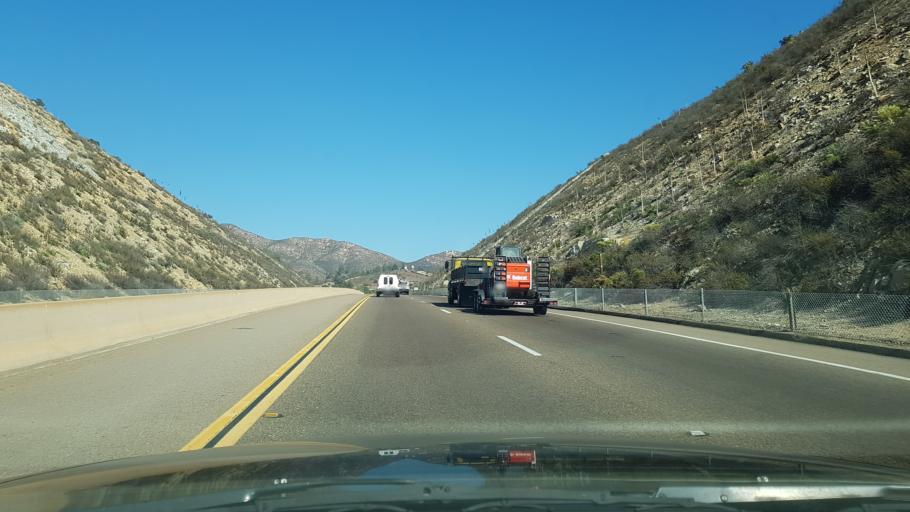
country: US
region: California
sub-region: San Diego County
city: Poway
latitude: 32.9522
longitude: -116.9749
